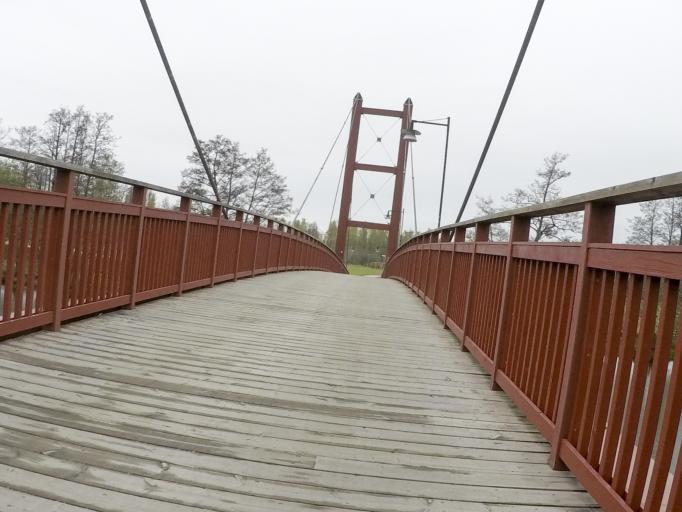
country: SE
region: Soedermanland
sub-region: Eskilstuna Kommun
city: Torshalla
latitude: 59.3830
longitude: 16.4759
